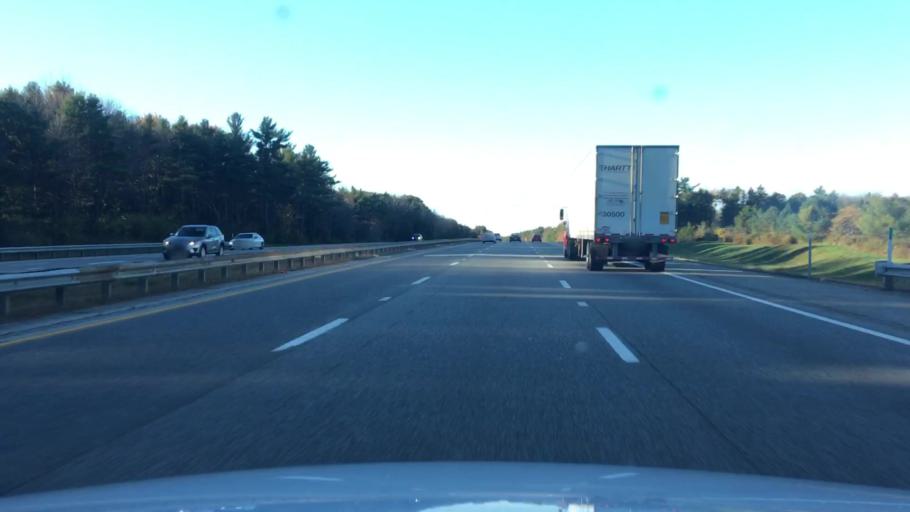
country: US
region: Maine
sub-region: York County
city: West Kennebunk
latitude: 43.4376
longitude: -70.5420
